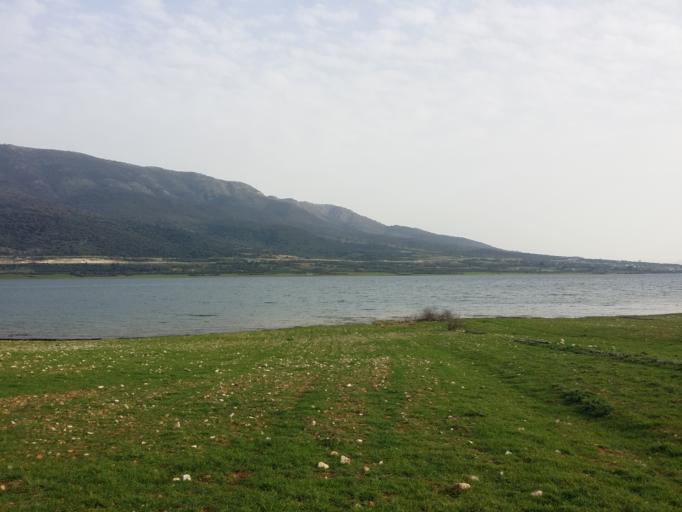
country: GR
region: West Greece
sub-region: Nomos Aitolias kai Akarnanias
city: Stanos
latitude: 38.7688
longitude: 21.1805
